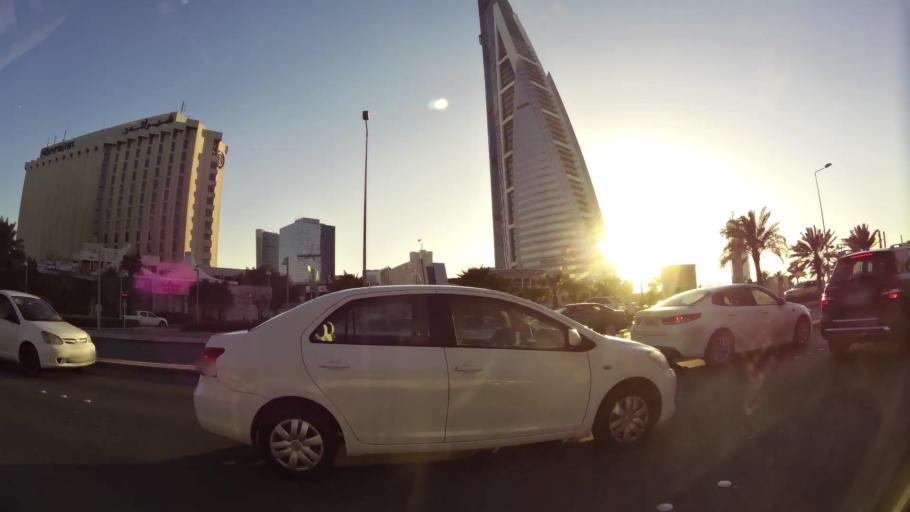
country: BH
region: Manama
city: Manama
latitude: 26.2404
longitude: 50.5837
